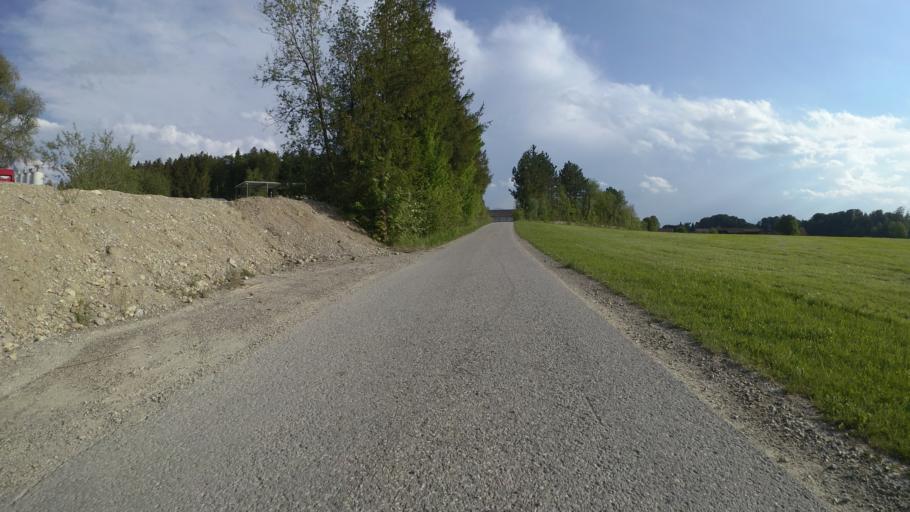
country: DE
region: Bavaria
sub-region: Upper Bavaria
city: Chieming
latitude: 47.8959
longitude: 12.5678
